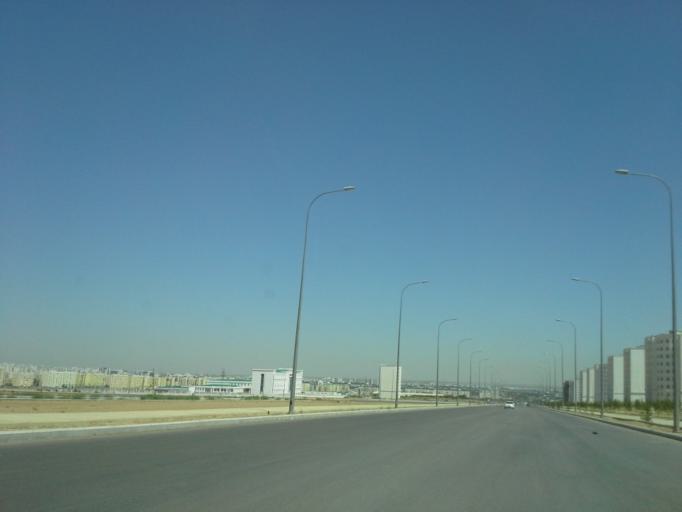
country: TM
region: Ahal
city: Ashgabat
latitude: 37.8879
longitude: 58.4055
